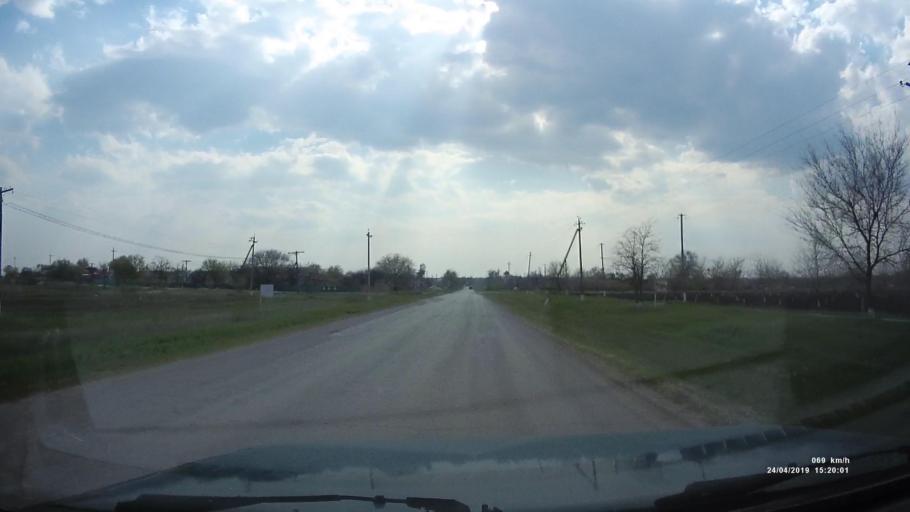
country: RU
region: Rostov
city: Remontnoye
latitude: 46.5372
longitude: 43.1381
